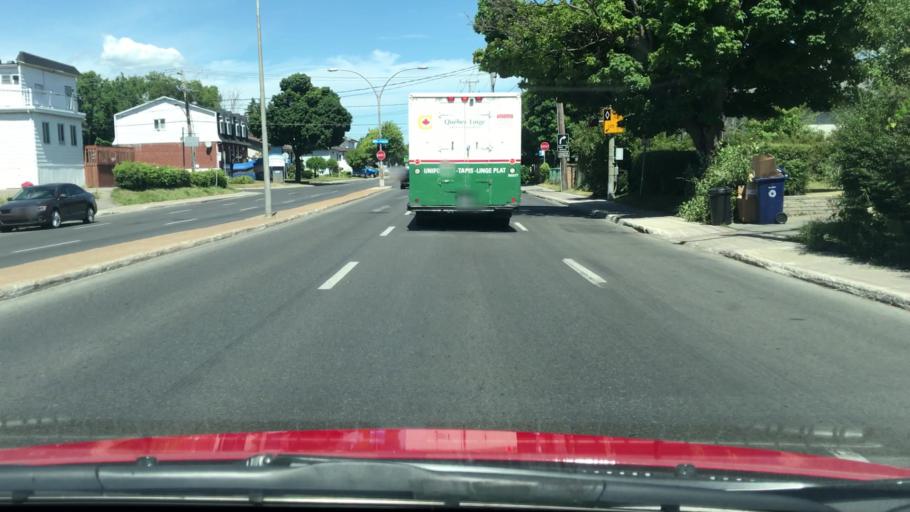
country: CA
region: Quebec
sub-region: Laval
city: Laval
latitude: 45.5353
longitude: -73.7472
